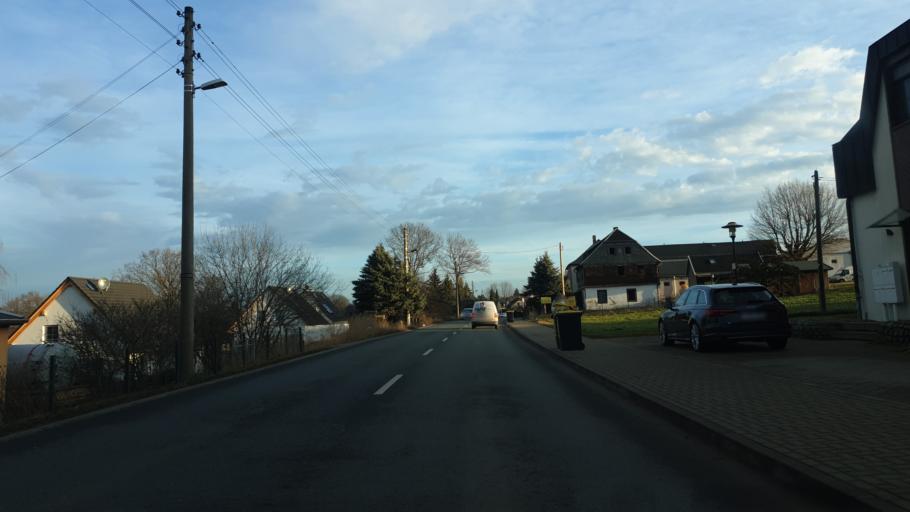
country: DE
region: Saxony
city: Neukirchen
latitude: 50.8012
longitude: 12.8037
